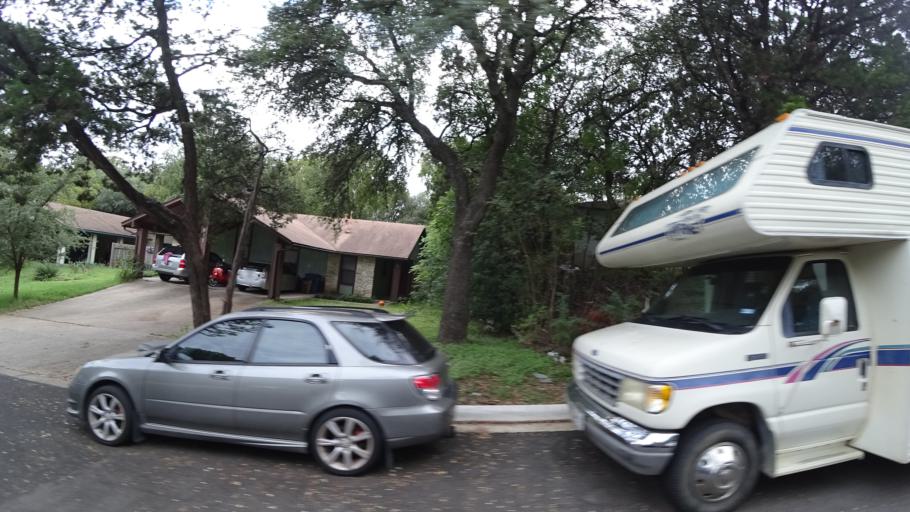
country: US
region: Texas
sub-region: Travis County
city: Rollingwood
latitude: 30.2122
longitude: -97.7833
